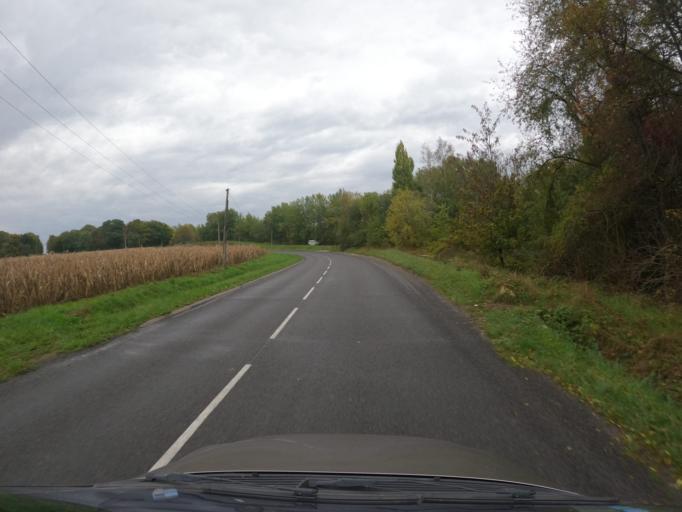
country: FR
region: Ile-de-France
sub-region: Departement de Seine-et-Marne
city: Serris
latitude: 48.8264
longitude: 2.7631
